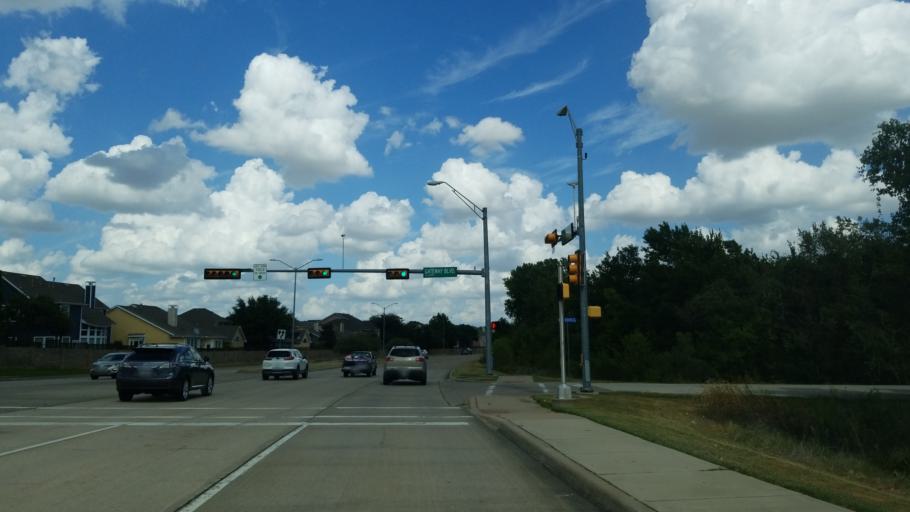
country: US
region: Texas
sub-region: Tarrant County
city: Euless
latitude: 32.8674
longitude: -97.0955
